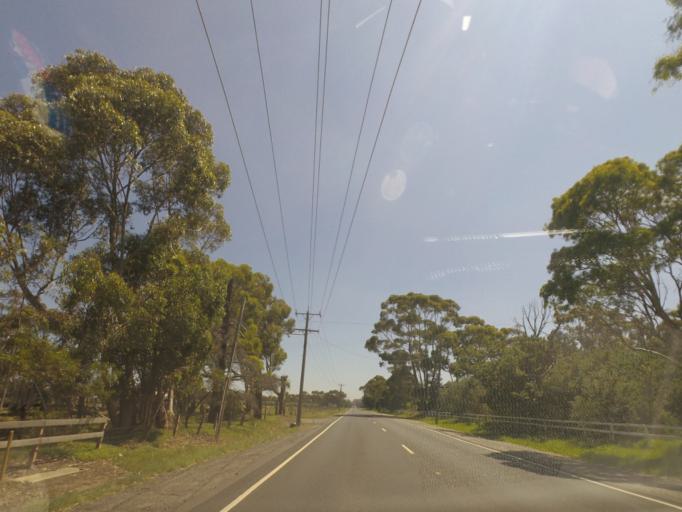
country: AU
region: Victoria
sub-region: Hume
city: Greenvale
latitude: -37.6265
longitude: 144.8371
